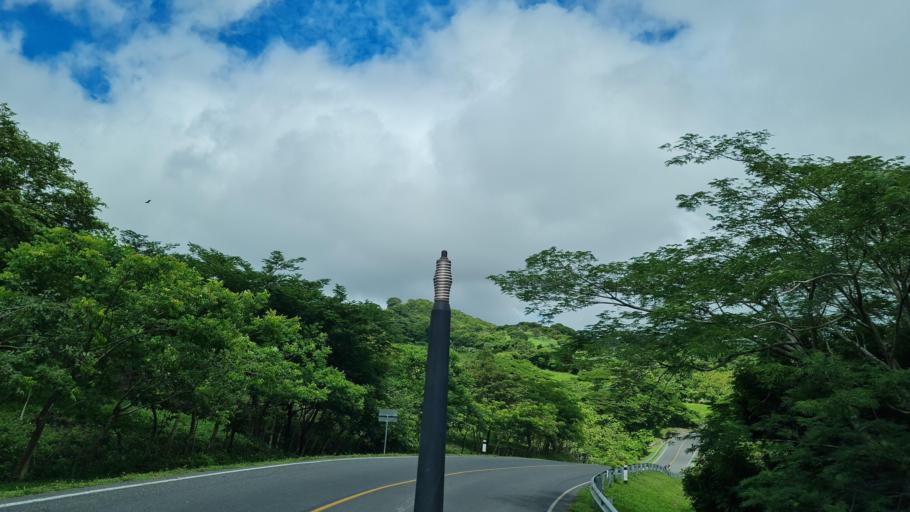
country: NI
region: Matagalpa
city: Terrabona
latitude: 12.5907
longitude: -85.9131
